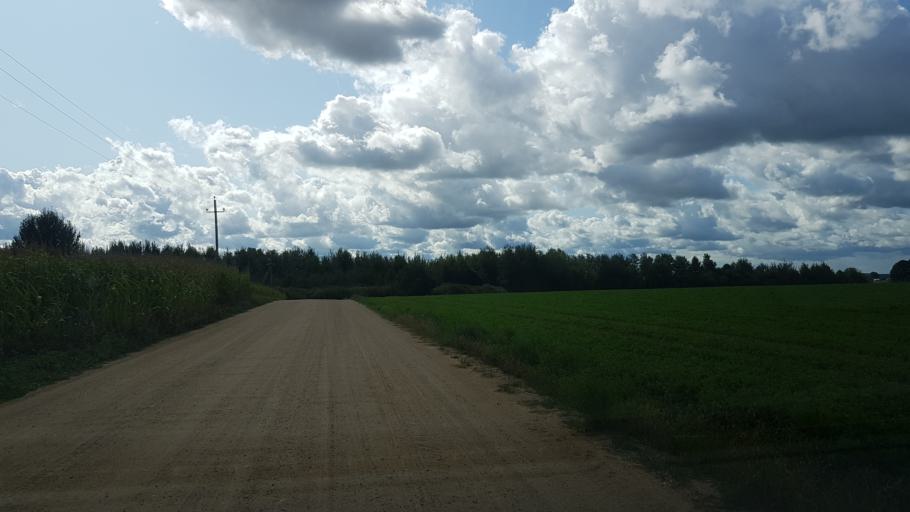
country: BY
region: Minsk
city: Dzyarzhynsk
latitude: 53.7494
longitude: 27.2095
